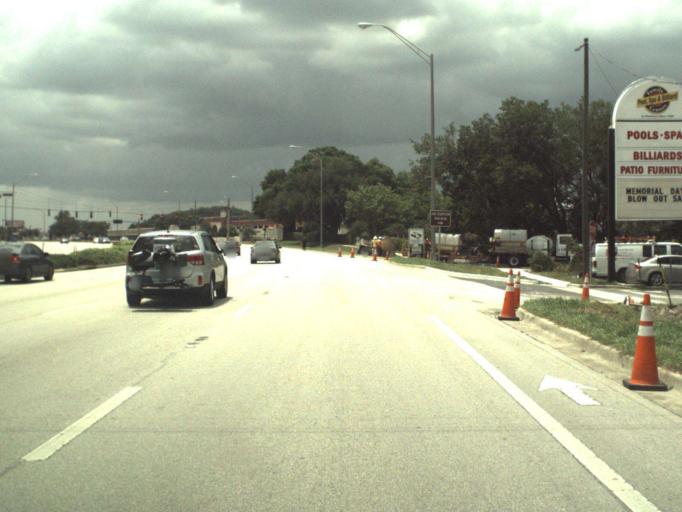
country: US
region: Florida
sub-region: Seminole County
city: Forest City
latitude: 28.6642
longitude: -81.4124
